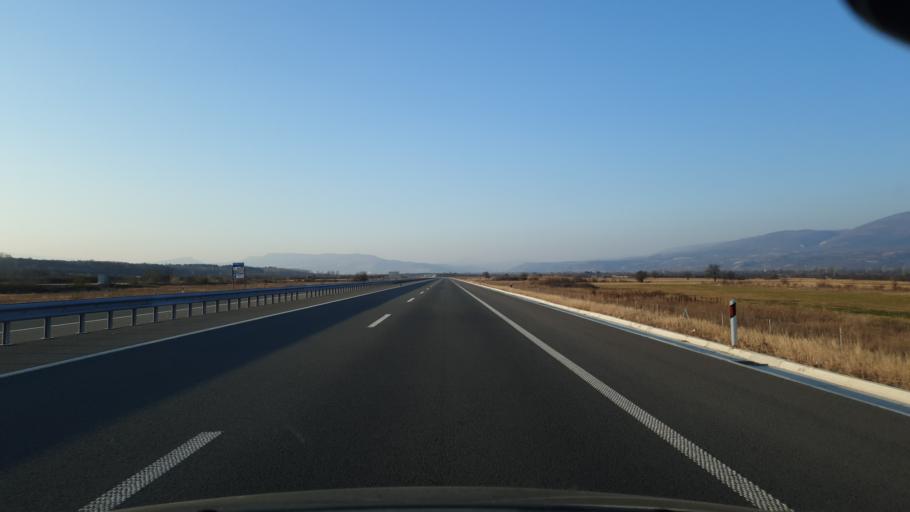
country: RS
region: Central Serbia
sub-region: Pirotski Okrug
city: Pirot
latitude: 43.0840
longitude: 22.6605
